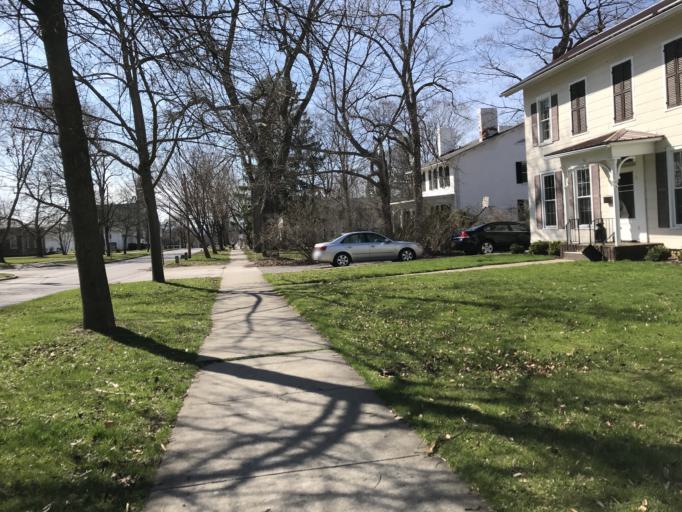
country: US
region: New York
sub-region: Livingston County
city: Geneseo
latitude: 42.7958
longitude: -77.8118
